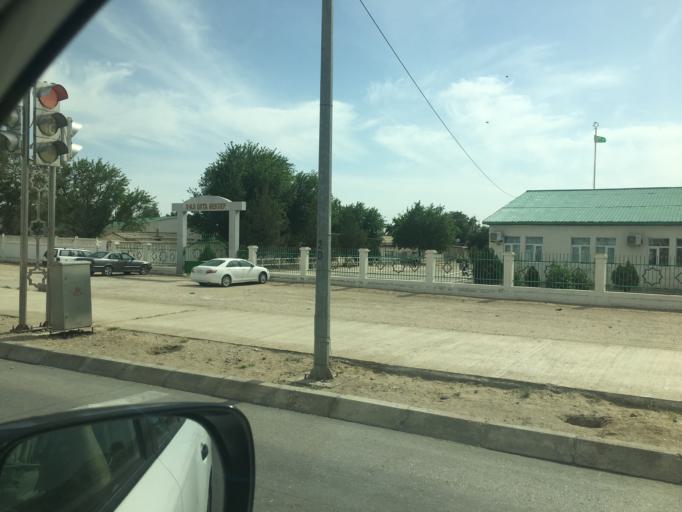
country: TM
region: Balkan
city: Balkanabat
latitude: 39.6342
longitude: 54.2346
